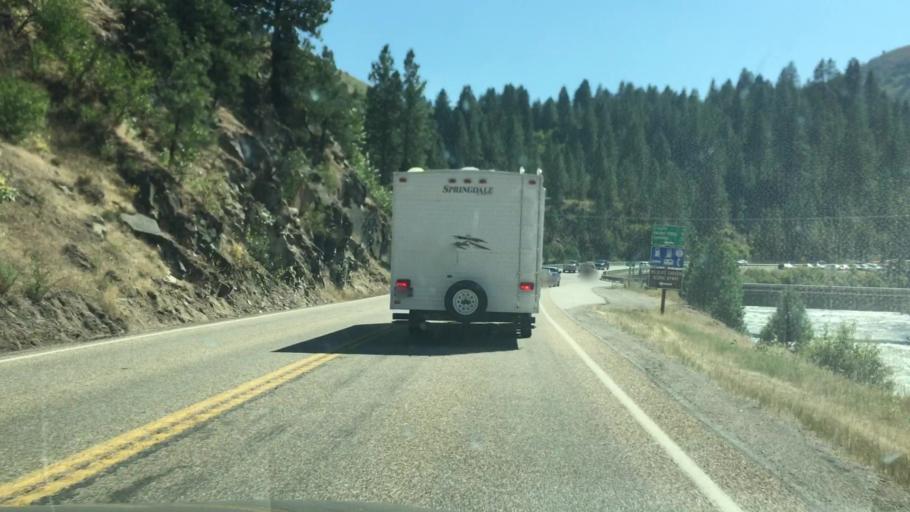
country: US
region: Idaho
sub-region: Boise County
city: Idaho City
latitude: 44.0856
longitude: -116.1139
